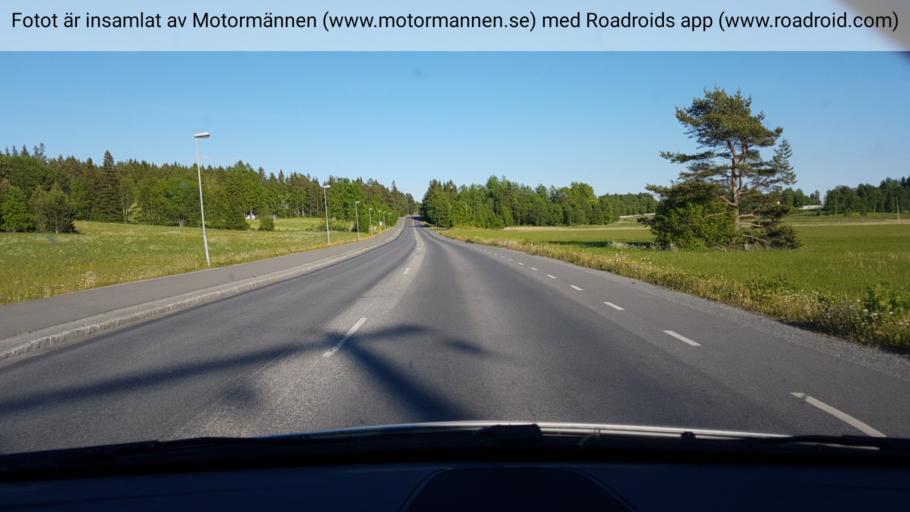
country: SE
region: Jaemtland
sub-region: OEstersunds Kommun
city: Ostersund
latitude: 63.1478
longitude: 14.7141
